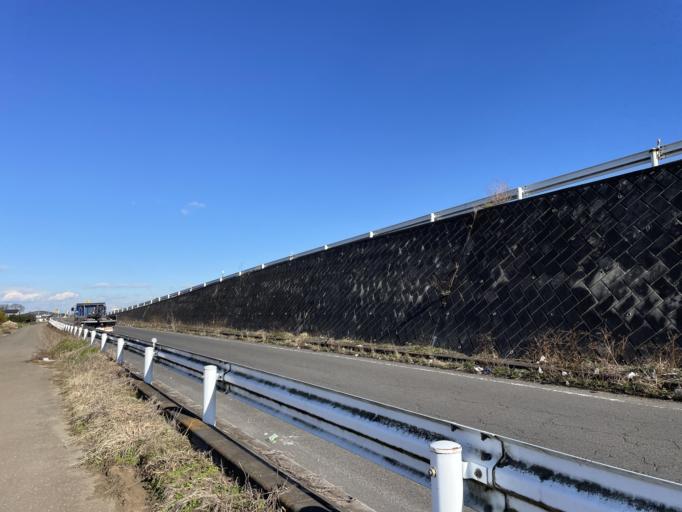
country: JP
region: Tochigi
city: Kaminokawa
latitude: 36.3892
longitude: 139.8741
